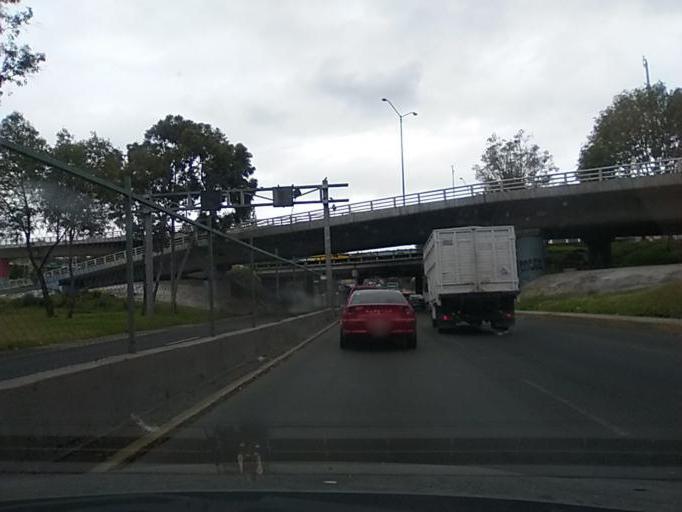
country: MX
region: Mexico City
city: Tlalpan
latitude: 19.2768
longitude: -99.1656
